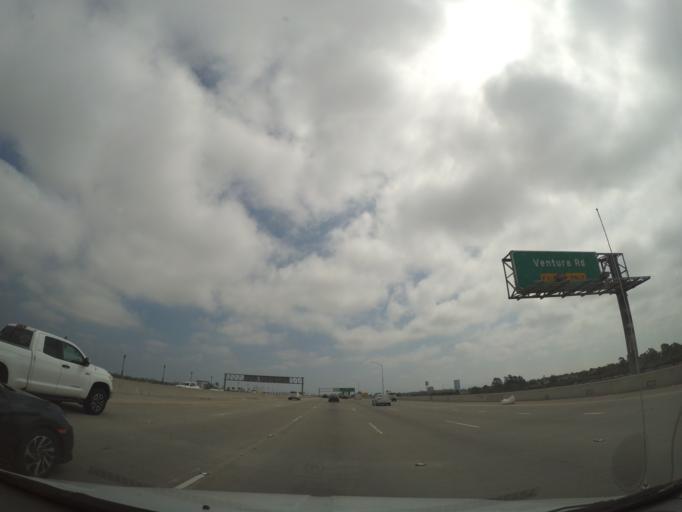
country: US
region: California
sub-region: Ventura County
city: El Rio
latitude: 34.2431
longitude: -119.1919
